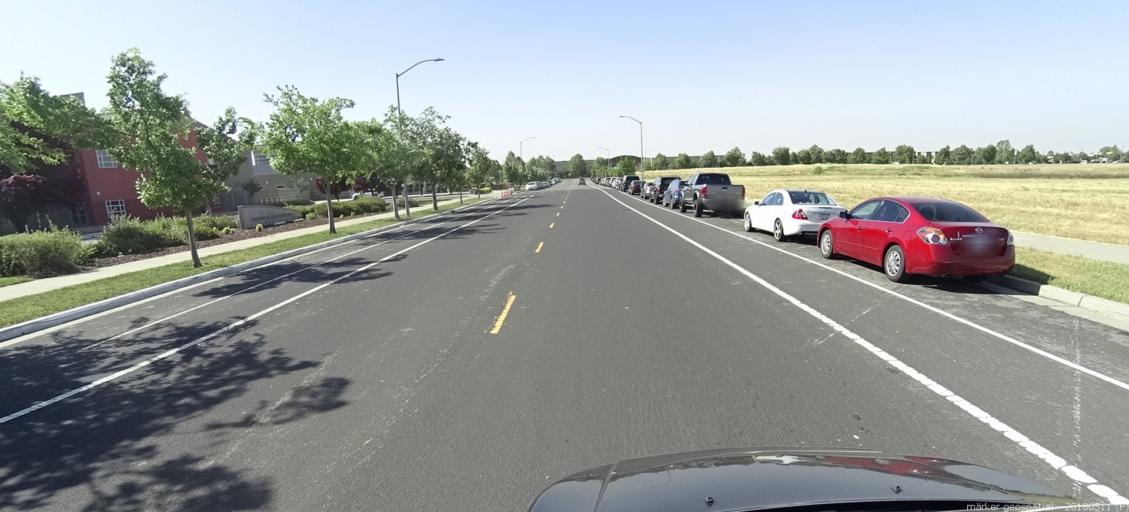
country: US
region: California
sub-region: Sacramento County
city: Rio Linda
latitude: 38.6586
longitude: -121.5186
